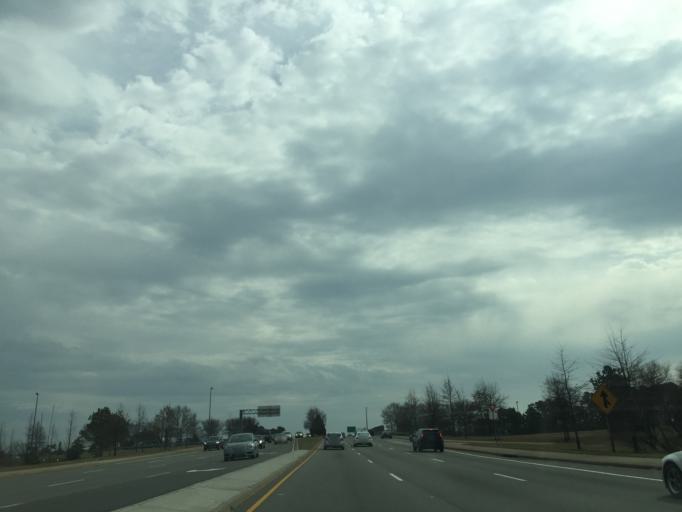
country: US
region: Virginia
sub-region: York County
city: Yorktown
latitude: 37.1187
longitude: -76.5045
